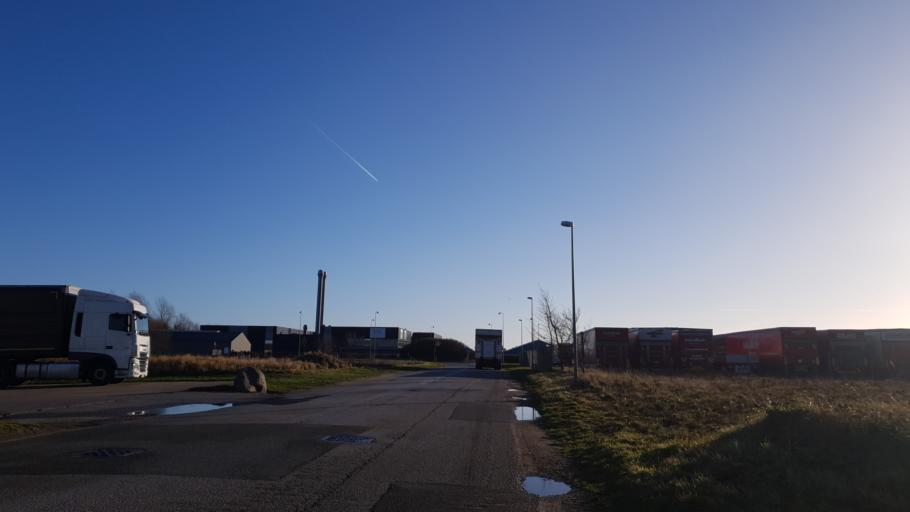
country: DK
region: Central Jutland
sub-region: Hedensted Kommune
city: Hedensted
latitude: 55.7922
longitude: 9.6741
